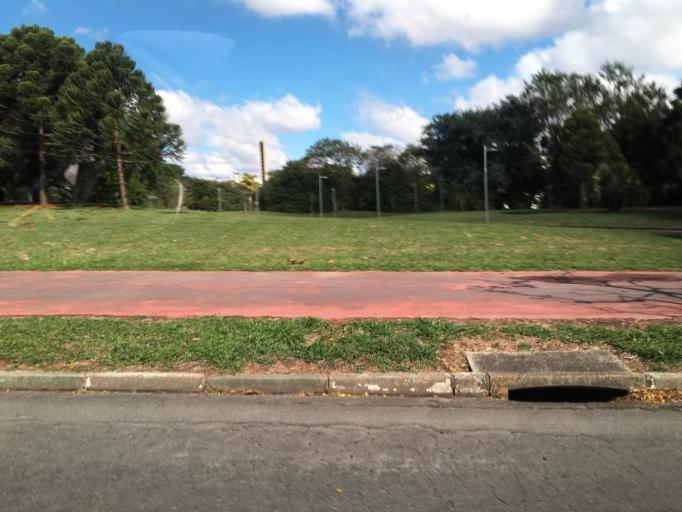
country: BR
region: Sao Paulo
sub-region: Osasco
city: Osasco
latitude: -23.5559
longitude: -46.7229
